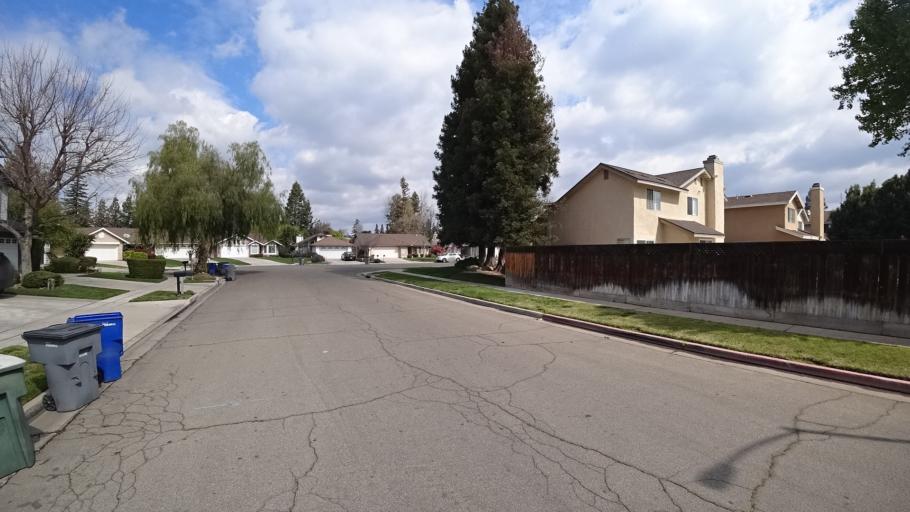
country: US
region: California
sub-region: Fresno County
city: Fresno
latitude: 36.8404
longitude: -119.8525
